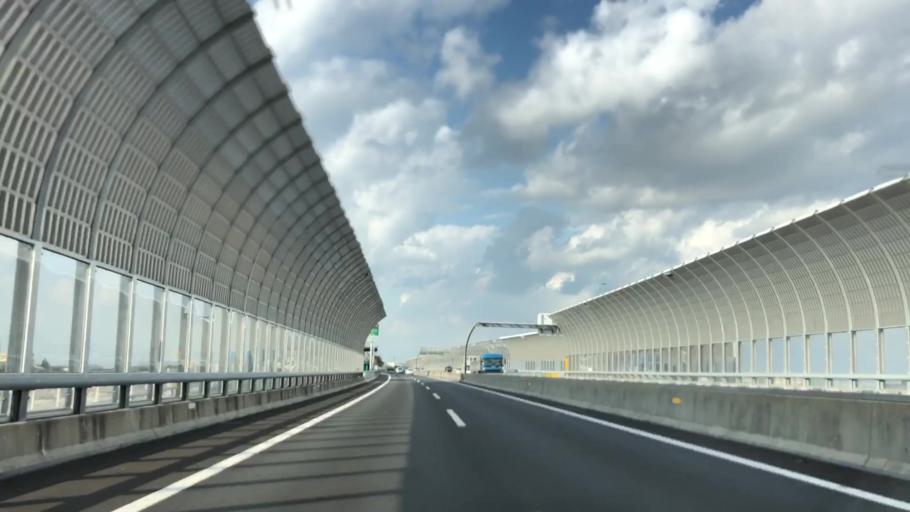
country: JP
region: Chiba
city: Matsudo
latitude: 35.8023
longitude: 139.8776
